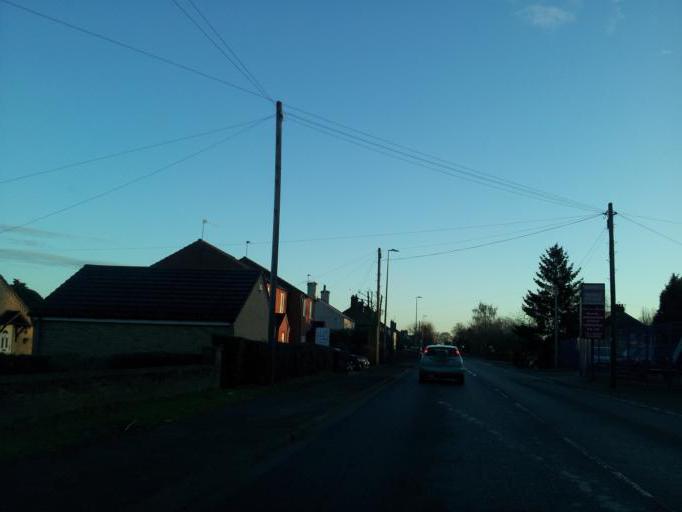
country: GB
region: England
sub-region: Lincolnshire
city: Sudbrooke
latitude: 53.2726
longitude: -0.4126
